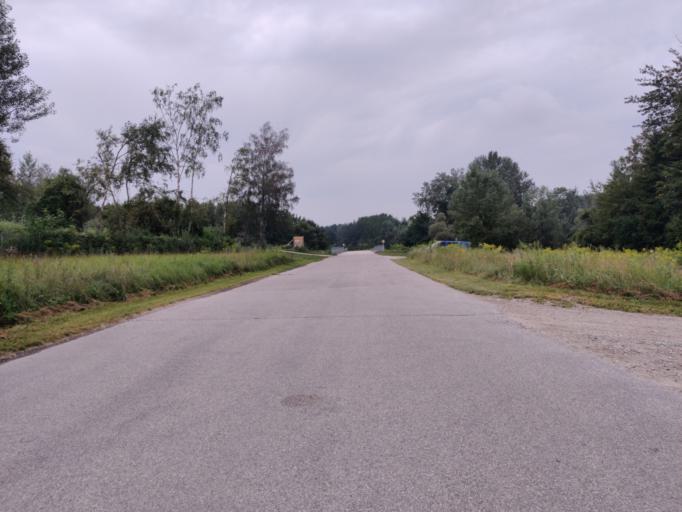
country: AT
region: Upper Austria
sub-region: Politischer Bezirk Linz-Land
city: Asten
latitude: 48.2433
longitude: 14.4264
